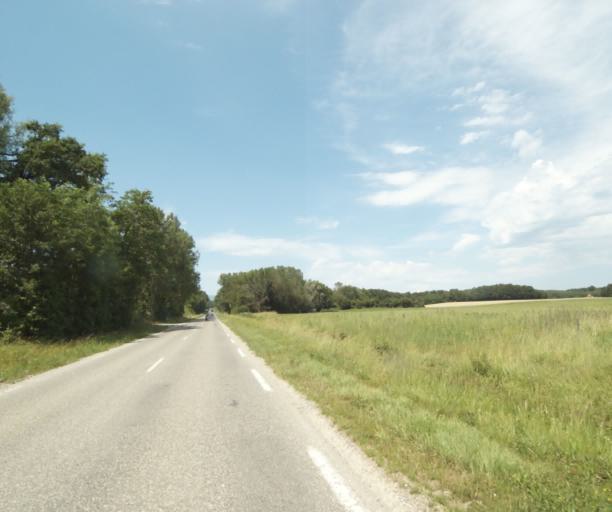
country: FR
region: Rhone-Alpes
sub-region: Departement de la Haute-Savoie
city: Douvaine
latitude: 46.3155
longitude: 6.2986
